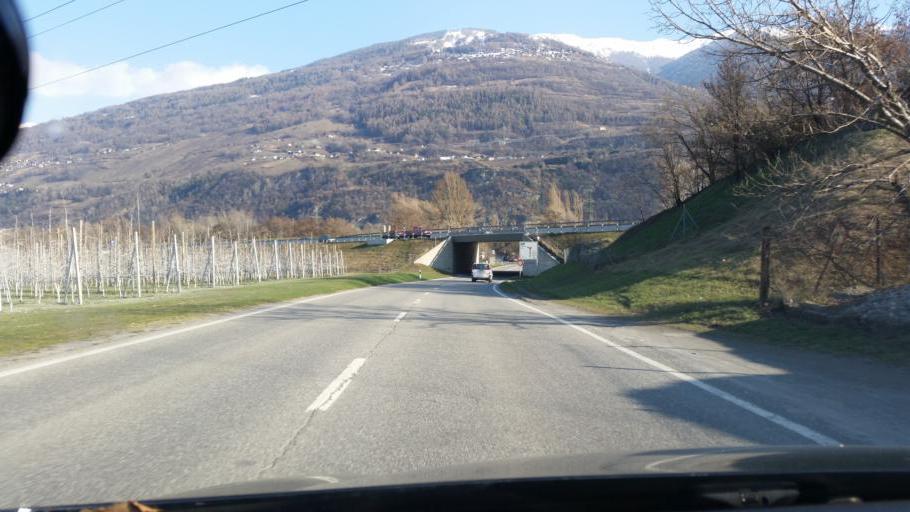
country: CH
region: Valais
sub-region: Conthey District
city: Conthey
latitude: 46.2138
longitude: 7.3088
